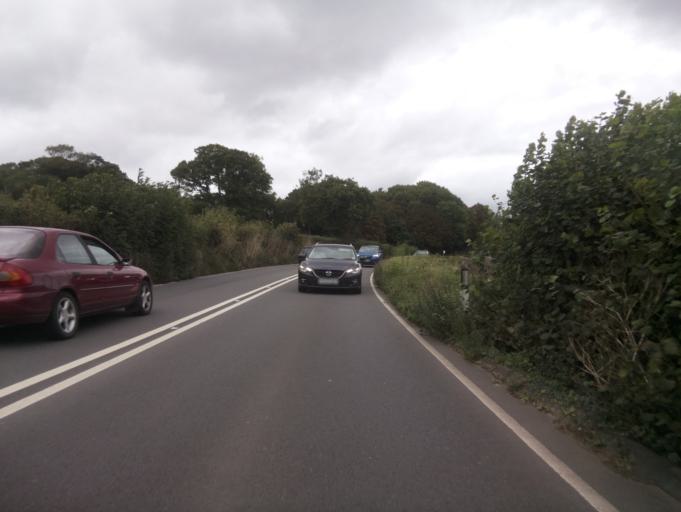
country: GB
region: England
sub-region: Devon
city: Kingsteignton
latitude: 50.5465
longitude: -3.5725
